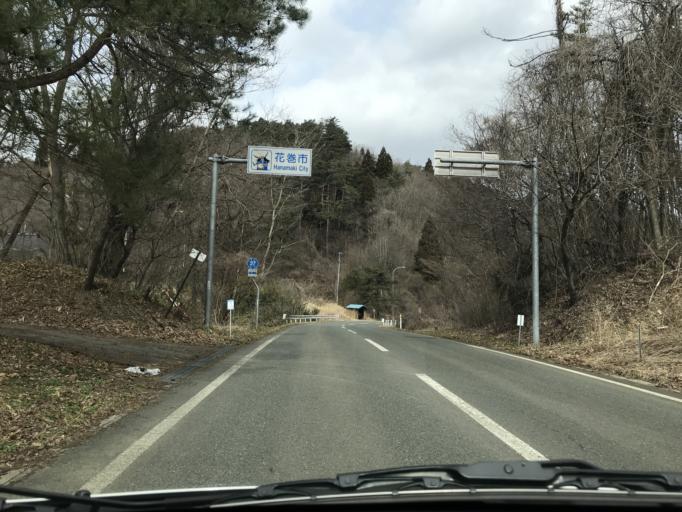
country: JP
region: Iwate
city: Kitakami
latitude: 39.2822
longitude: 141.3189
